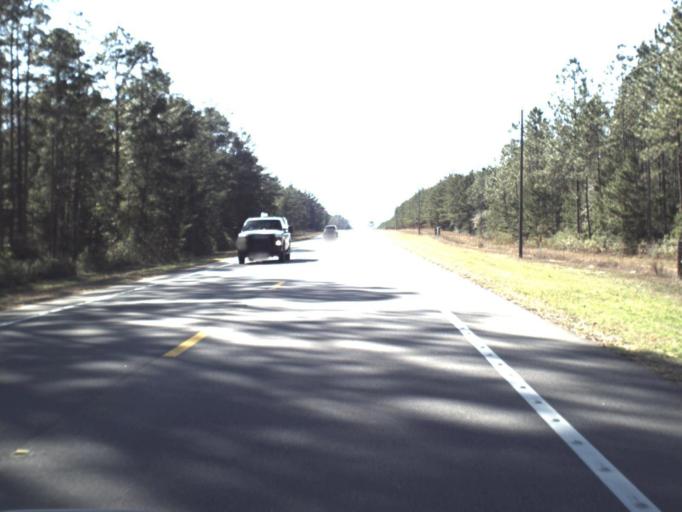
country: US
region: Florida
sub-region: Bay County
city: Youngstown
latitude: 30.4338
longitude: -85.2544
